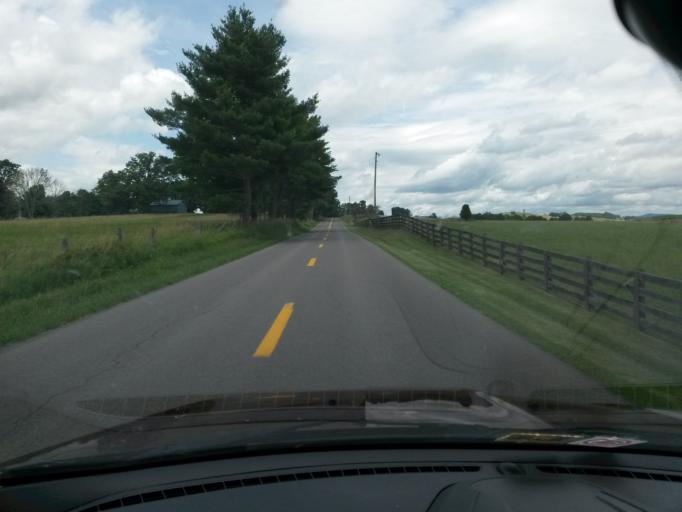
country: US
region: West Virginia
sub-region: Monroe County
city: Union
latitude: 37.5449
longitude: -80.5338
